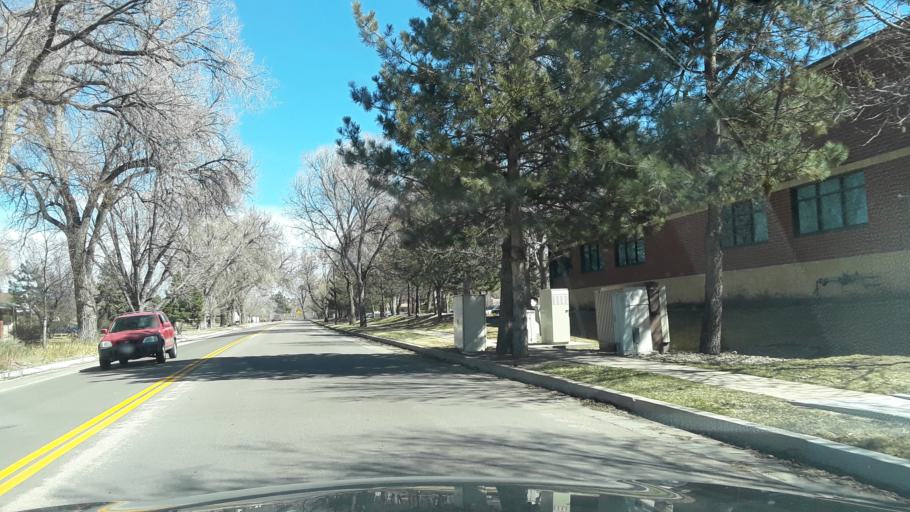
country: US
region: Colorado
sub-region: El Paso County
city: Colorado Springs
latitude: 38.8751
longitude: -104.7977
